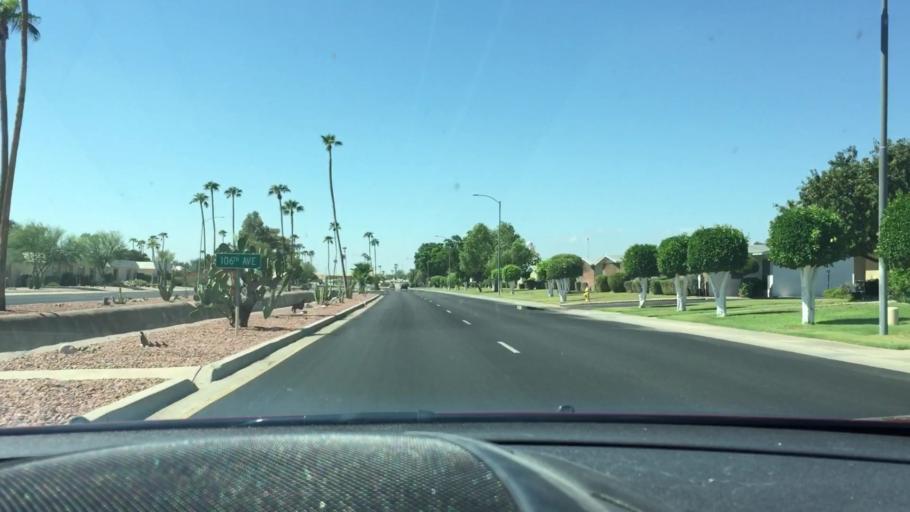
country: US
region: Arizona
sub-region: Maricopa County
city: Sun City
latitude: 33.6429
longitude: -112.2849
